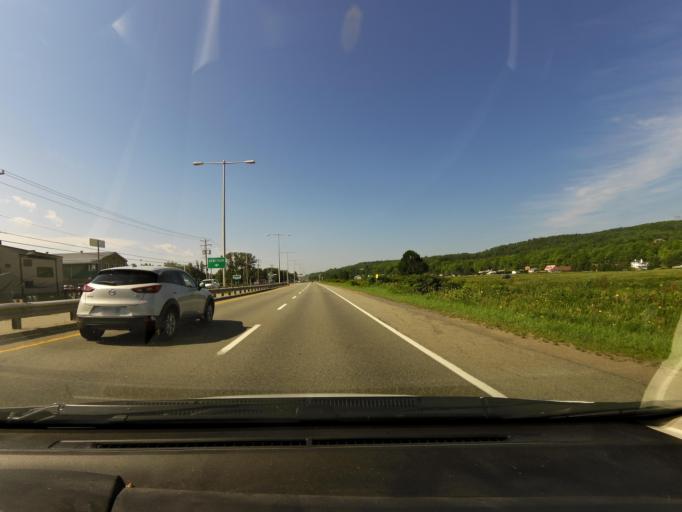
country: CA
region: Quebec
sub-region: Capitale-Nationale
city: Chateau-Richer
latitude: 46.9864
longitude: -70.9956
